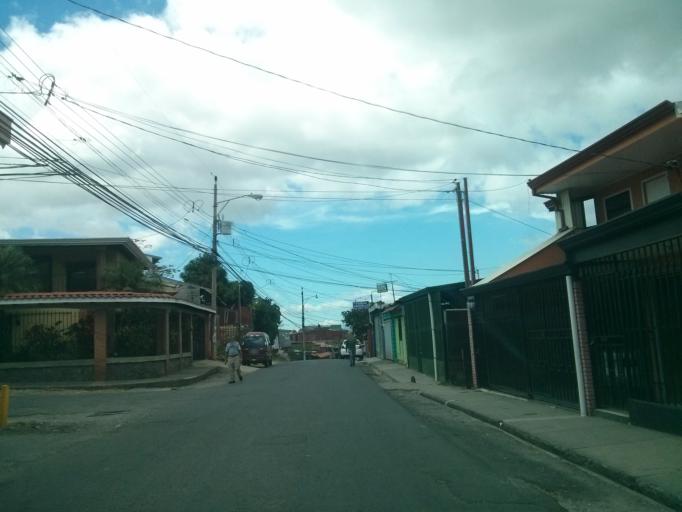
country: CR
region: San Jose
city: San Rafael Arriba
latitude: 9.8813
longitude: -84.0749
